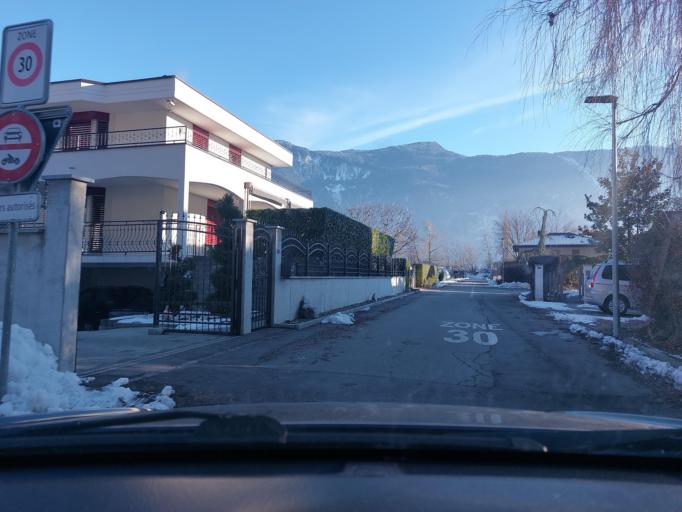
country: CH
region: Valais
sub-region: Martigny District
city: Fully
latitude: 46.1303
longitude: 7.1009
